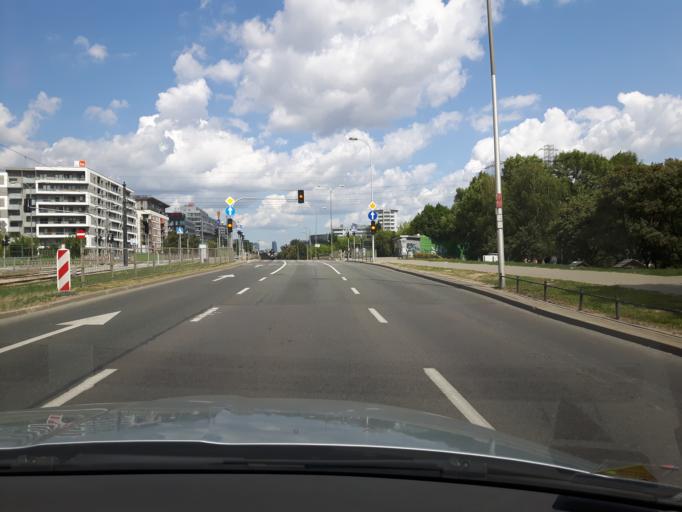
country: PL
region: Masovian Voivodeship
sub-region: Warszawa
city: Wlochy
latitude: 52.1964
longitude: 20.9639
